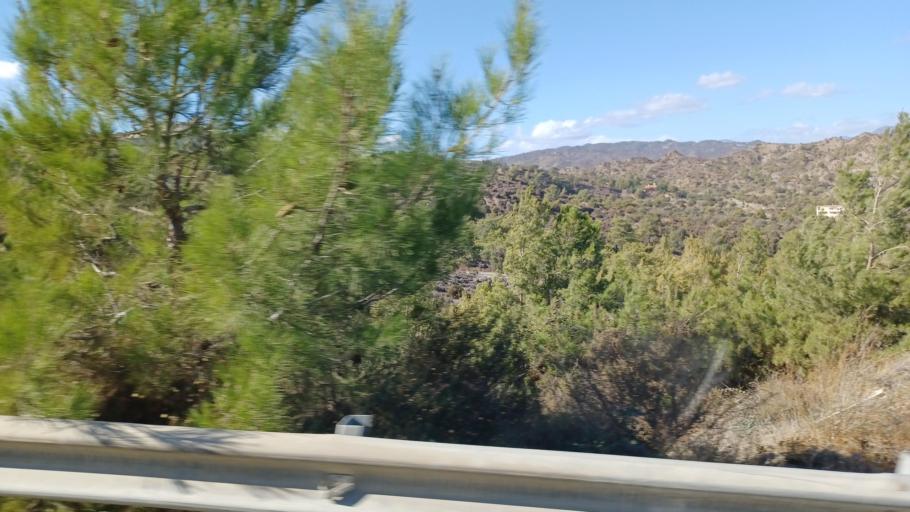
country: CY
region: Limassol
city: Pyrgos
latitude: 34.7726
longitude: 33.2471
